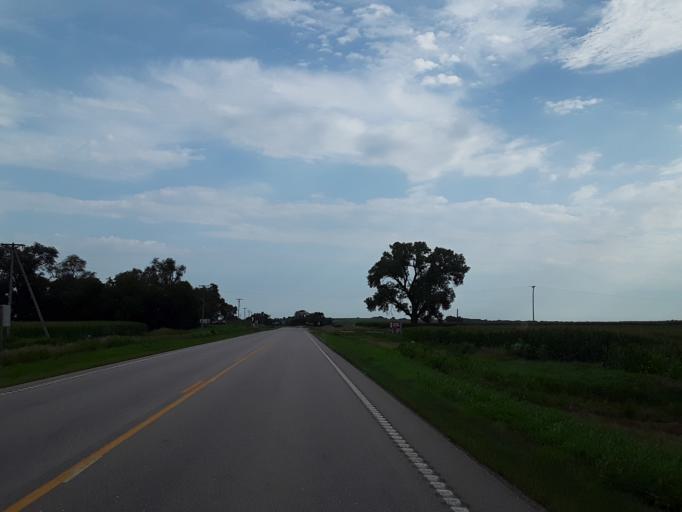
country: US
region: Nebraska
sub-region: Saunders County
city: Ashland
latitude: 41.0977
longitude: -96.4259
